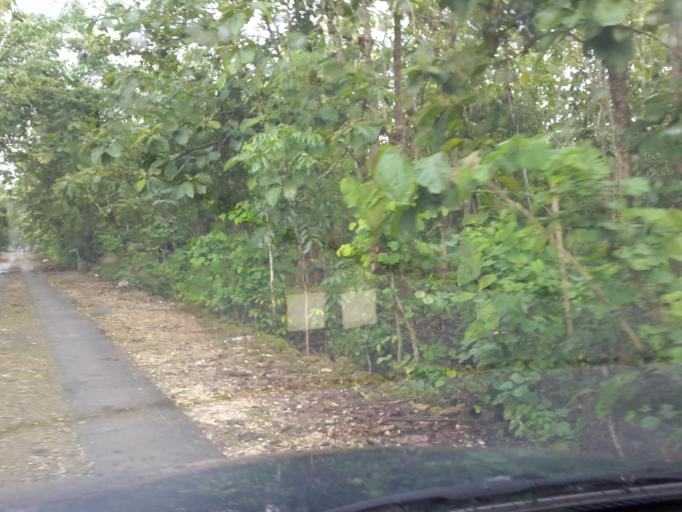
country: ID
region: Daerah Istimewa Yogyakarta
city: Wonosari
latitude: -7.9703
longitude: 110.6391
